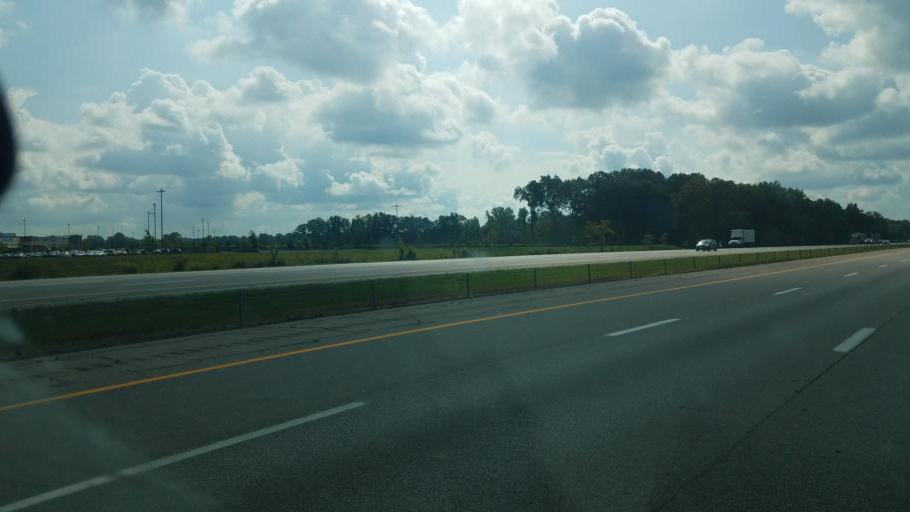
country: US
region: Ohio
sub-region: Delaware County
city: Sunbury
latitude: 40.2602
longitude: -82.9282
